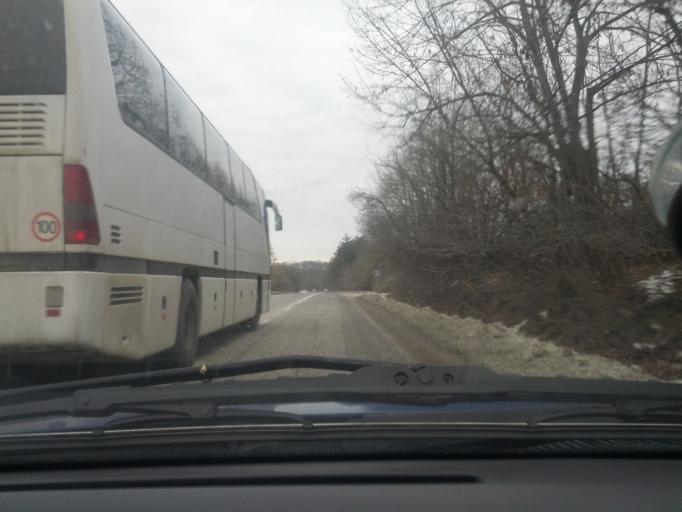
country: BG
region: Vratsa
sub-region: Obshtina Vratsa
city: Vratsa
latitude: 43.2573
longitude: 23.5869
